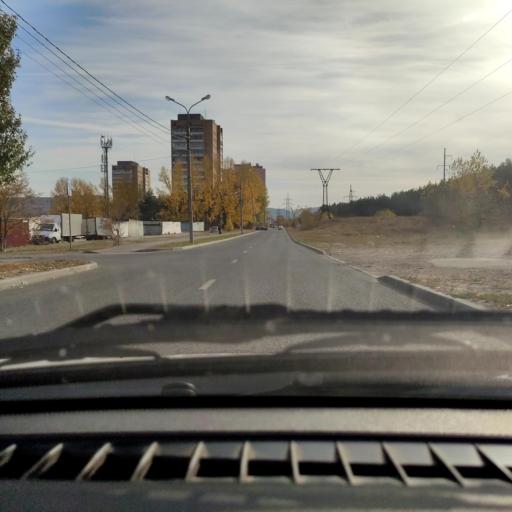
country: RU
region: Samara
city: Zhigulevsk
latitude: 53.4805
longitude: 49.4542
